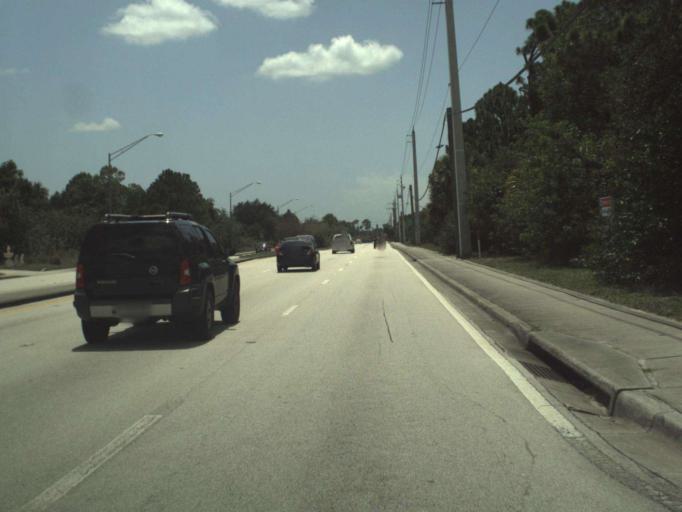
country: US
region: Florida
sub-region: Saint Lucie County
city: Port Saint Lucie
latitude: 27.2706
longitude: -80.3640
